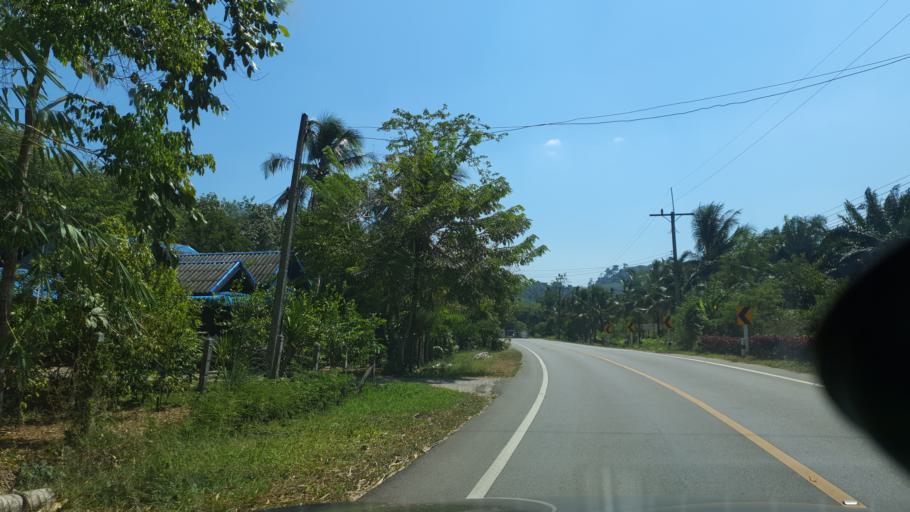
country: TH
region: Krabi
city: Khlong Thom
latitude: 7.9345
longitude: 99.2206
